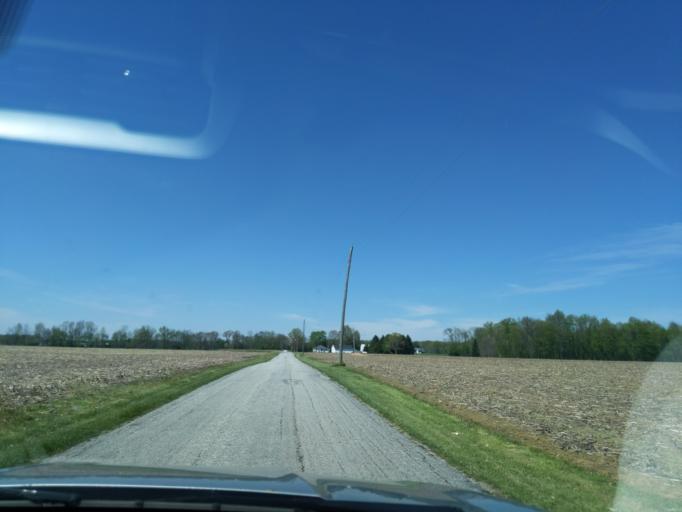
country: US
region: Indiana
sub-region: Decatur County
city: Greensburg
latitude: 39.2451
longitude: -85.4335
